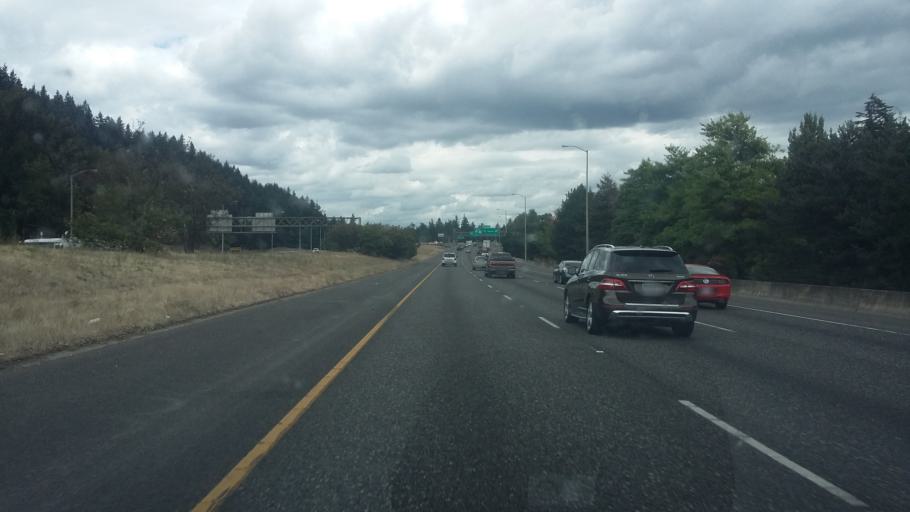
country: US
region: Oregon
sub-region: Multnomah County
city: Lents
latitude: 45.5391
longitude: -122.5629
